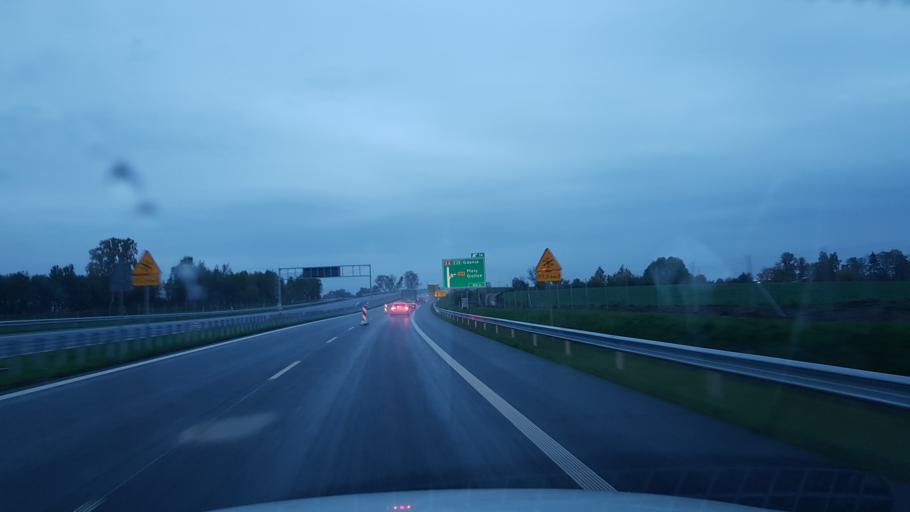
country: PL
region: West Pomeranian Voivodeship
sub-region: Powiat gryficki
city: Ploty
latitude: 53.8095
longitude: 15.2477
